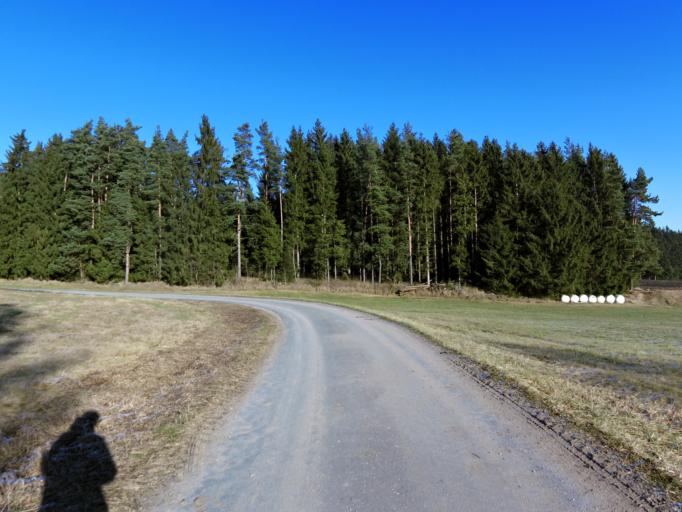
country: DE
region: Bavaria
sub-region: Upper Franconia
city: Roslau
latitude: 50.0725
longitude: 12.0084
